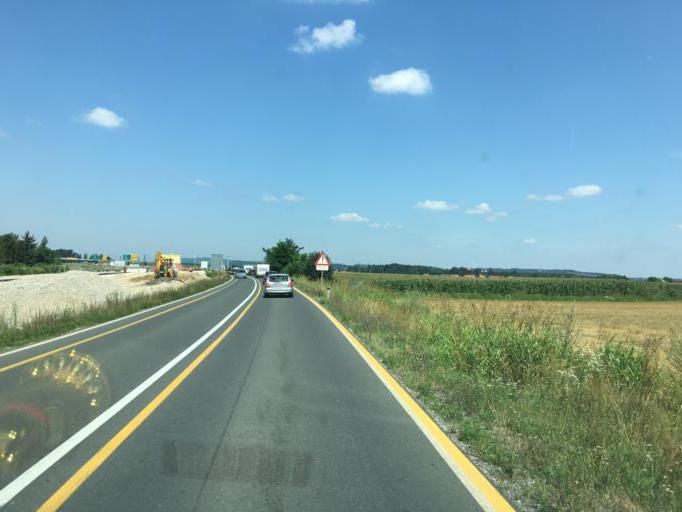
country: SI
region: Hajdina
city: Spodnja Hajdina
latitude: 46.3844
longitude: 15.8653
